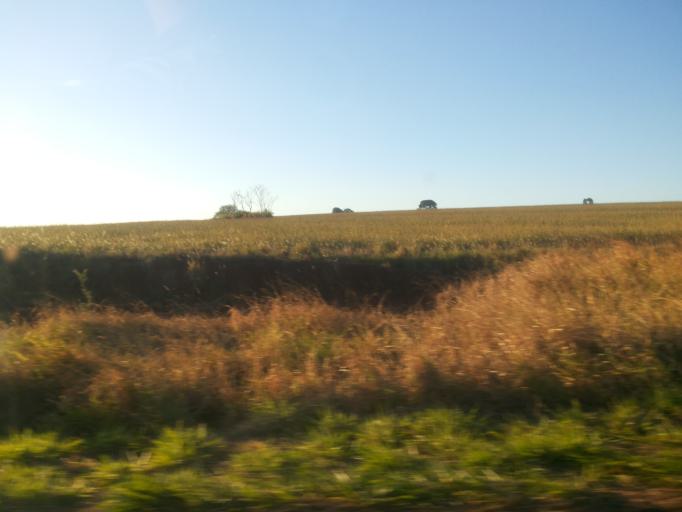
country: BR
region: Minas Gerais
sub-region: Centralina
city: Centralina
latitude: -18.7336
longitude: -49.2500
